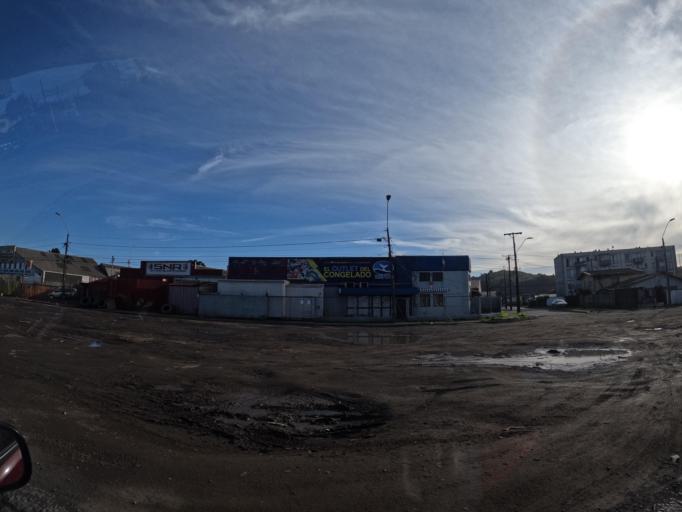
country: CL
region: Biobio
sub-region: Provincia de Concepcion
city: Talcahuano
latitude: -36.7704
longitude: -73.0832
